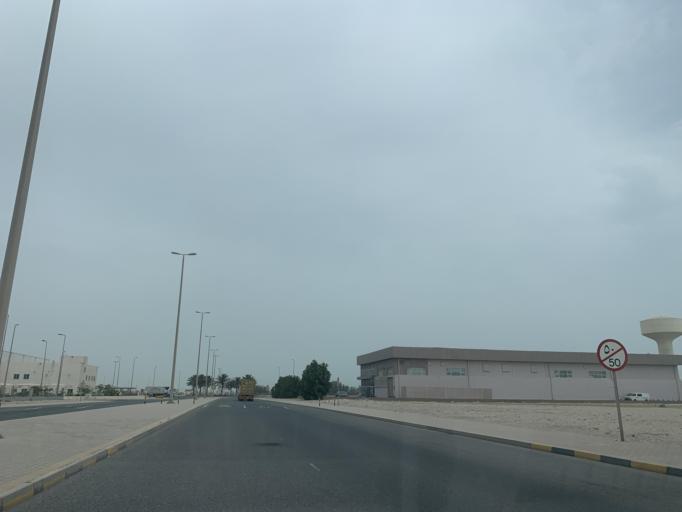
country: BH
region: Muharraq
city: Al Hadd
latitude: 26.2188
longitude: 50.6795
